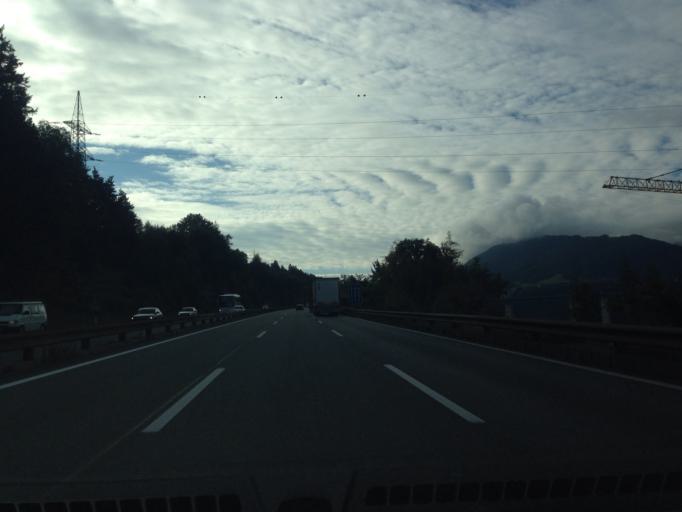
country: AT
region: Tyrol
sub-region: Politischer Bezirk Innsbruck Land
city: Mutters
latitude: 47.2148
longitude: 11.3977
